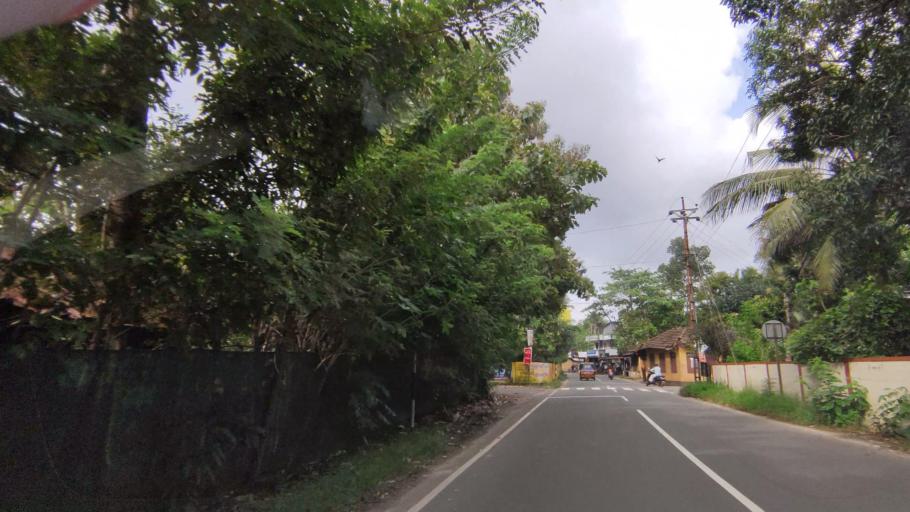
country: IN
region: Kerala
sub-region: Alappuzha
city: Shertallai
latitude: 9.6013
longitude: 76.3578
